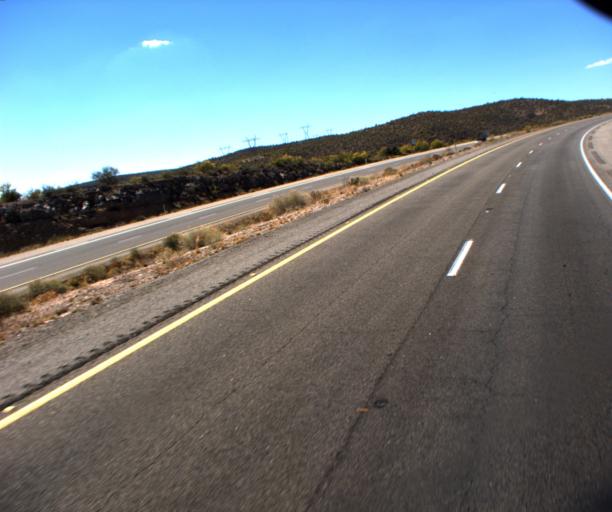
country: US
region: Arizona
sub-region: Yavapai County
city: Bagdad
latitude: 34.5480
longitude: -113.4505
